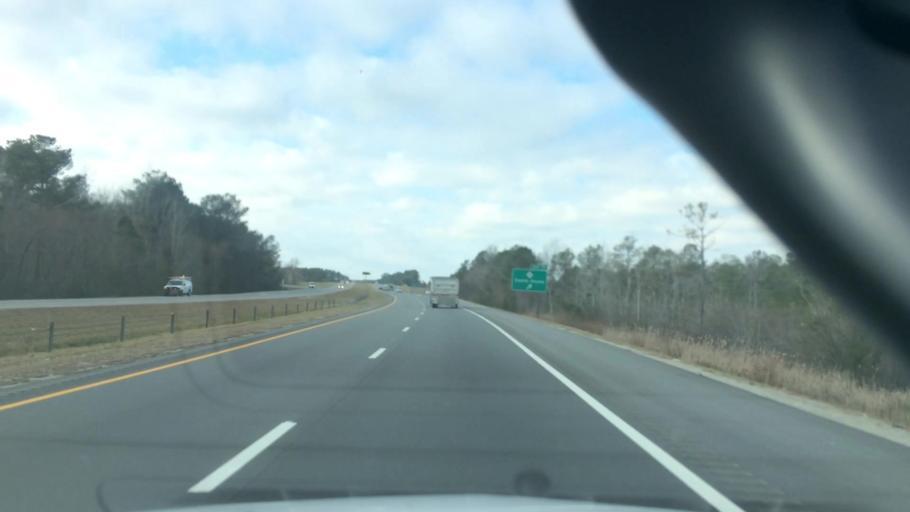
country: US
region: North Carolina
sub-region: New Hanover County
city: Wrightsboro
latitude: 34.3154
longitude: -77.9141
